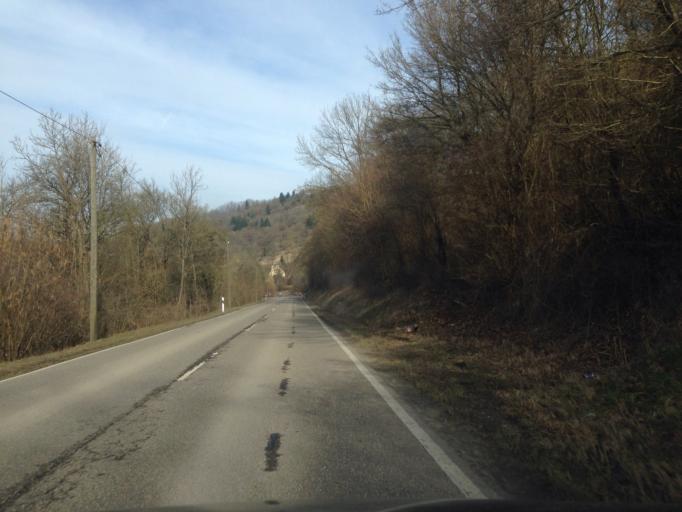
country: DE
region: Baden-Wuerttemberg
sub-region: Regierungsbezirk Stuttgart
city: Widdern
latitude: 49.3131
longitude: 9.4316
